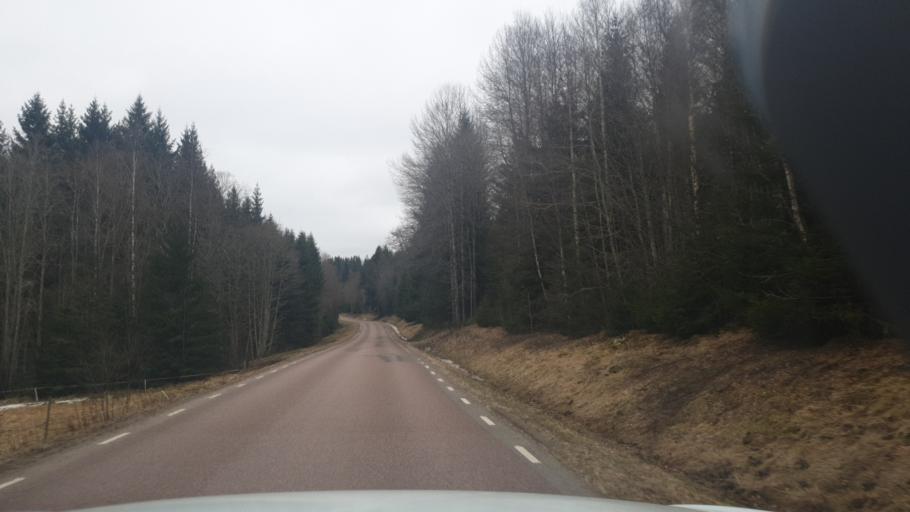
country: NO
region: Ostfold
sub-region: Romskog
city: Romskog
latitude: 59.7474
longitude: 12.0550
